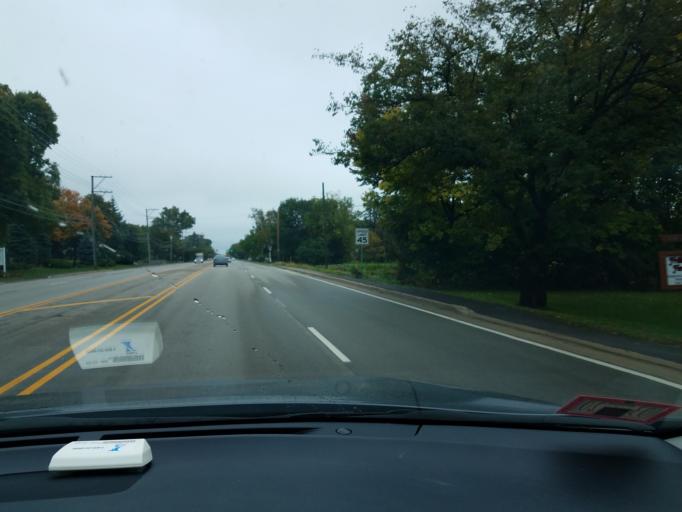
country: US
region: Illinois
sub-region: Cook County
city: Buffalo Grove
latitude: 42.1826
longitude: -87.9602
